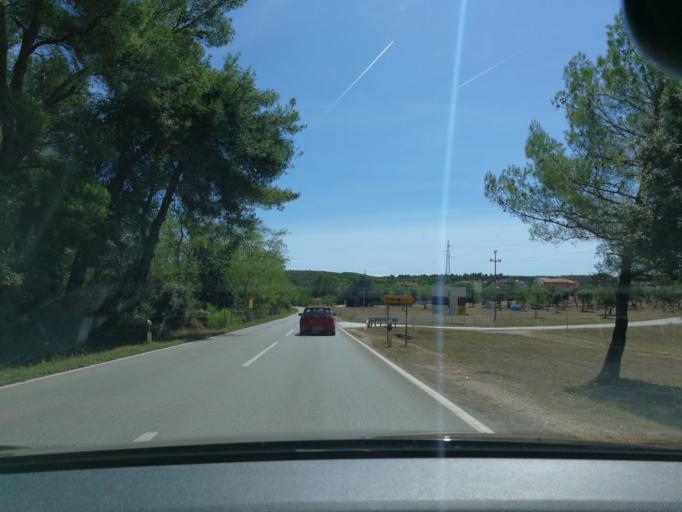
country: HR
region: Istarska
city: Medulin
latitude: 44.8222
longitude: 13.8802
